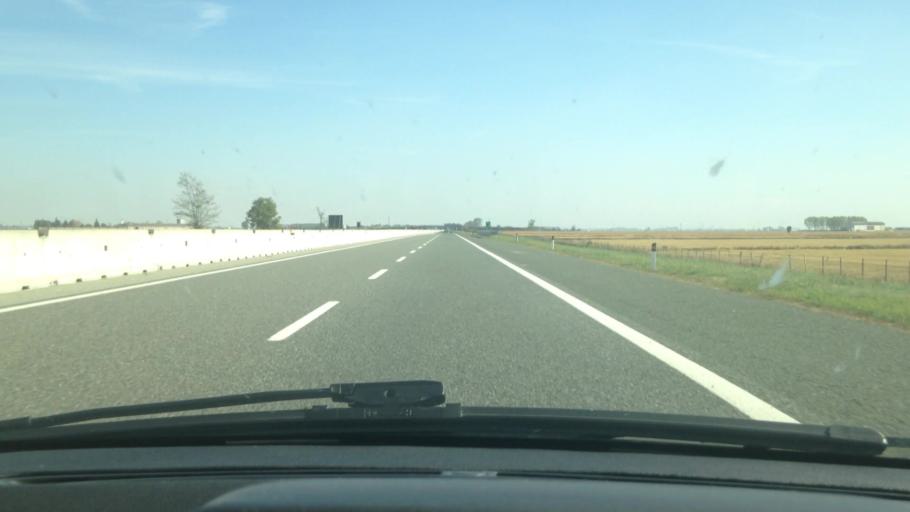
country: IT
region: Piedmont
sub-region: Provincia di Vercelli
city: Salasco
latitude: 45.3149
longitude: 8.2727
